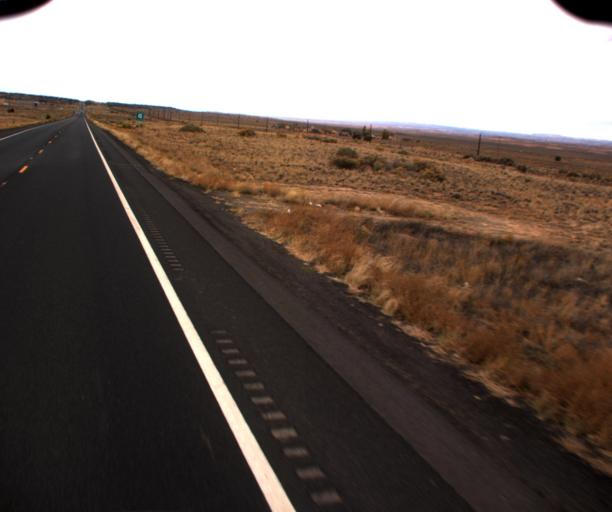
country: US
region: Arizona
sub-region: Coconino County
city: Kaibito
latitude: 36.4649
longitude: -110.6833
